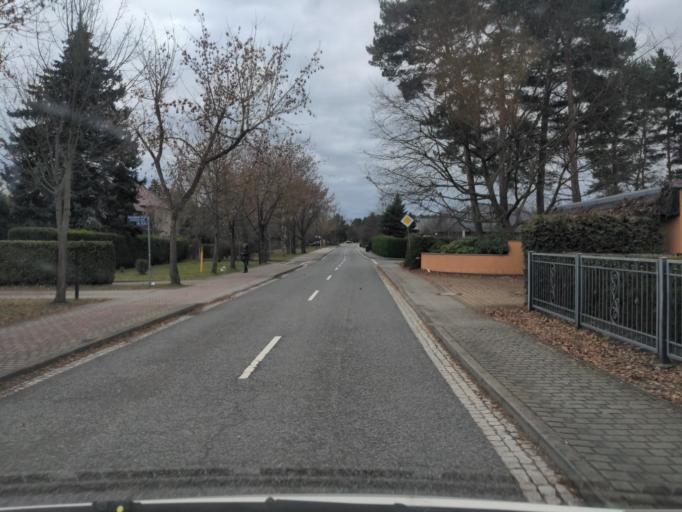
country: DE
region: Brandenburg
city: Cottbus
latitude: 51.7112
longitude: 14.3347
